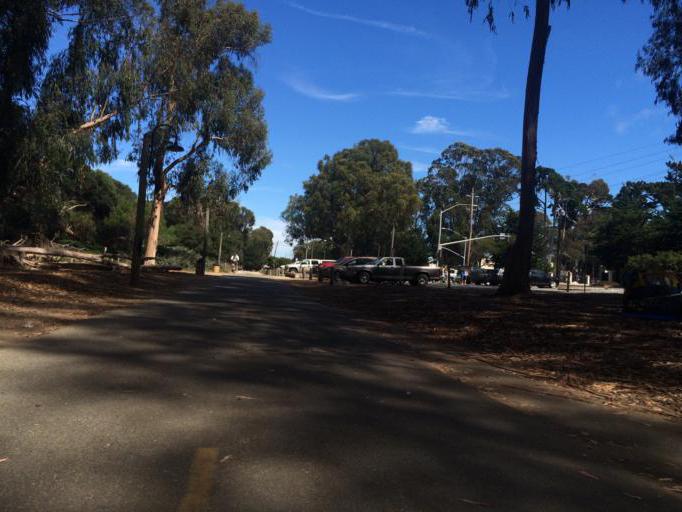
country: US
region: California
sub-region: Monterey County
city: Monterey
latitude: 36.6003
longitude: -121.8754
